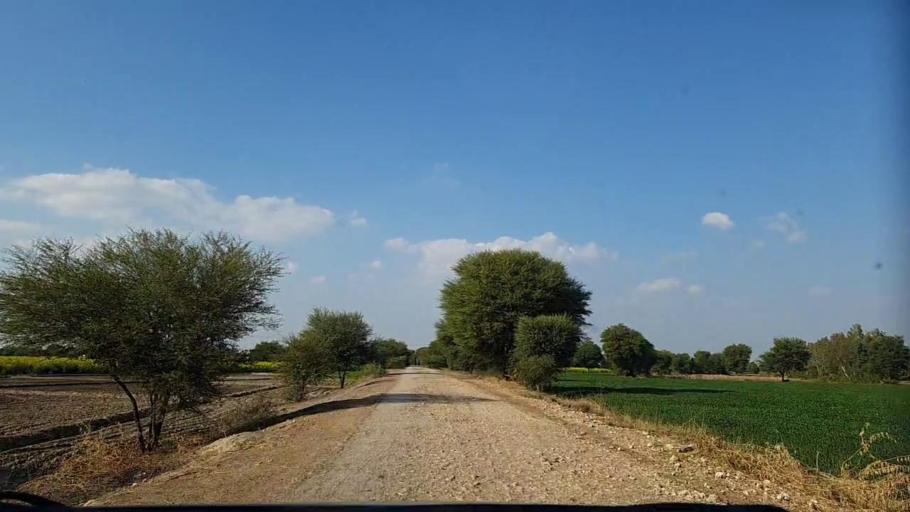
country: PK
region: Sindh
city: Pithoro
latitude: 25.6406
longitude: 69.3505
